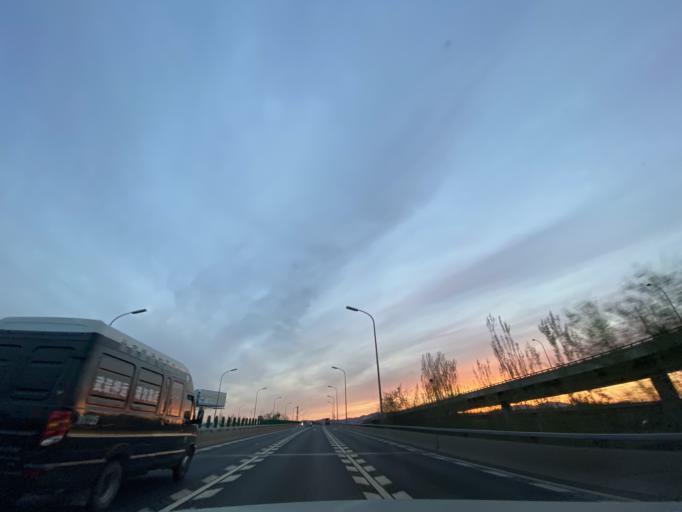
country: CN
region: Beijing
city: Qinghe
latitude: 40.0195
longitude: 116.3220
